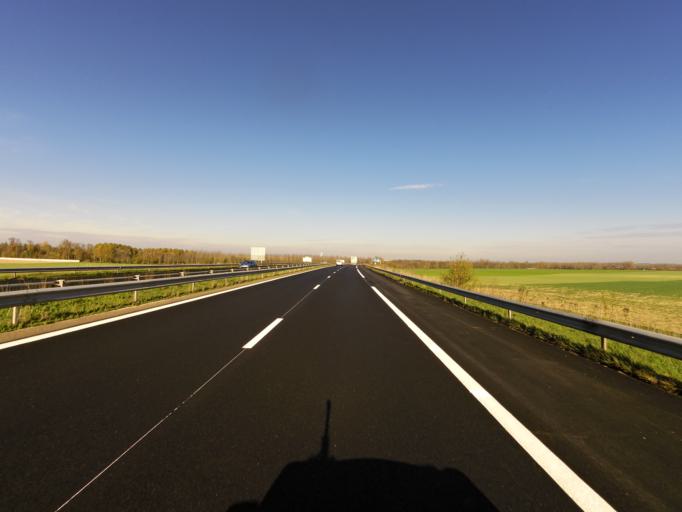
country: FR
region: Champagne-Ardenne
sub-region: Departement de la Marne
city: Fagnieres
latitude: 48.9615
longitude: 4.2862
